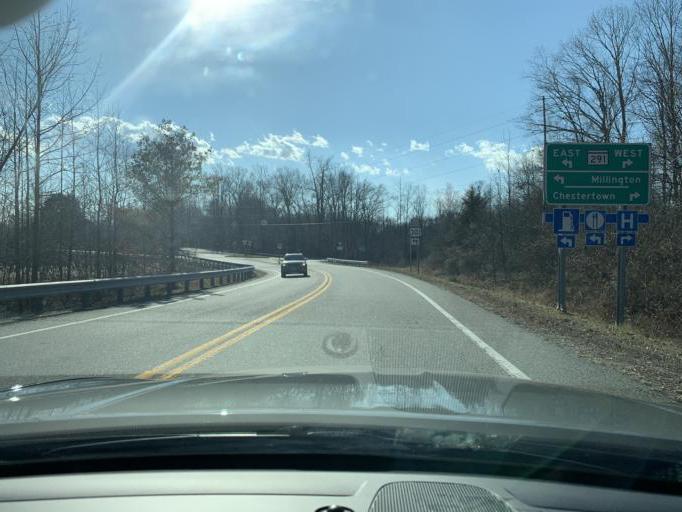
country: US
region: Maryland
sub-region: Queen Anne's County
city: Kingstown
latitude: 39.2656
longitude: -75.8658
